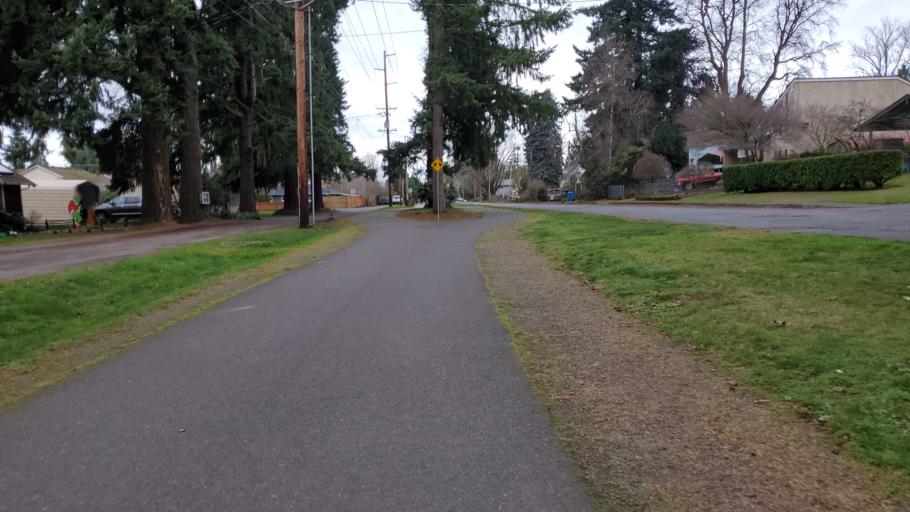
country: US
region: Oregon
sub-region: Clackamas County
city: Jennings Lodge
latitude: 45.3875
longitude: -122.6073
